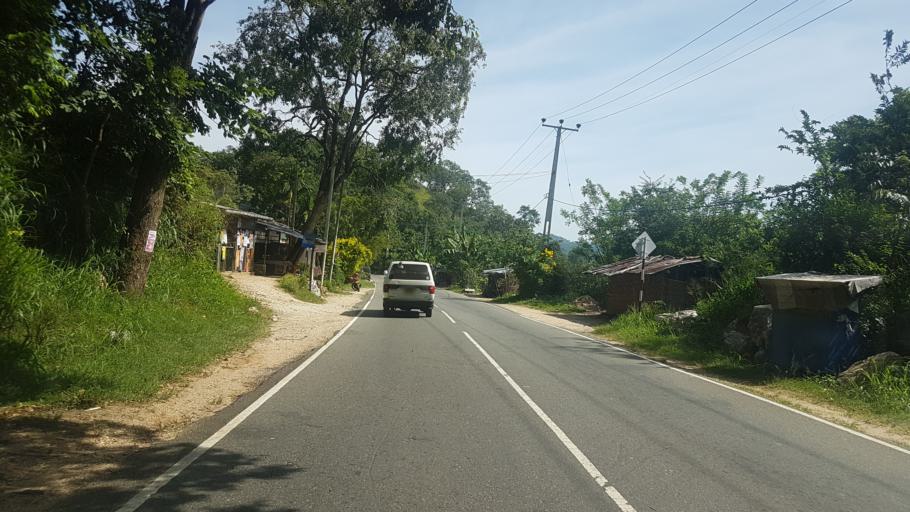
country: LK
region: Uva
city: Haputale
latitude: 6.8017
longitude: 81.0952
